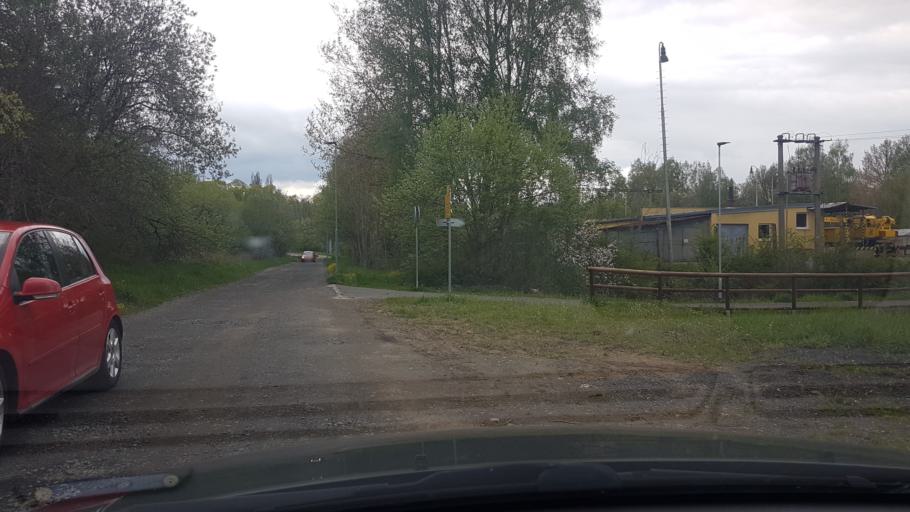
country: CZ
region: Karlovarsky
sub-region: Okres Cheb
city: Cheb
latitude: 50.0581
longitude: 12.3846
